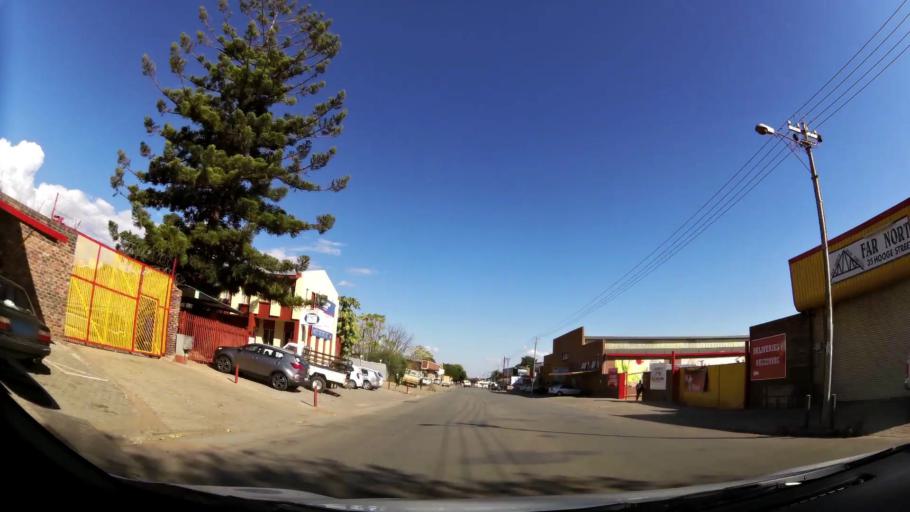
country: ZA
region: Limpopo
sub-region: Waterberg District Municipality
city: Mokopane
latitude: -24.1801
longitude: 29.0164
